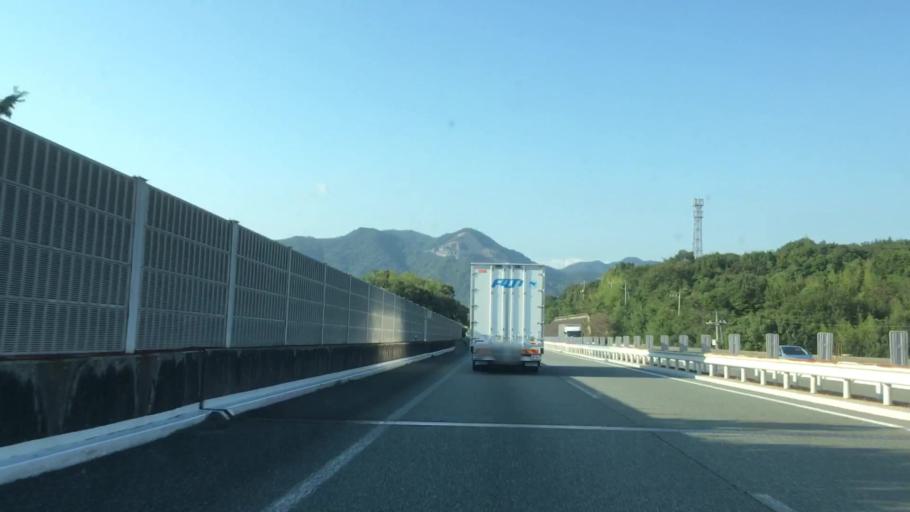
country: JP
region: Yamaguchi
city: Hofu
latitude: 34.0621
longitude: 131.5022
